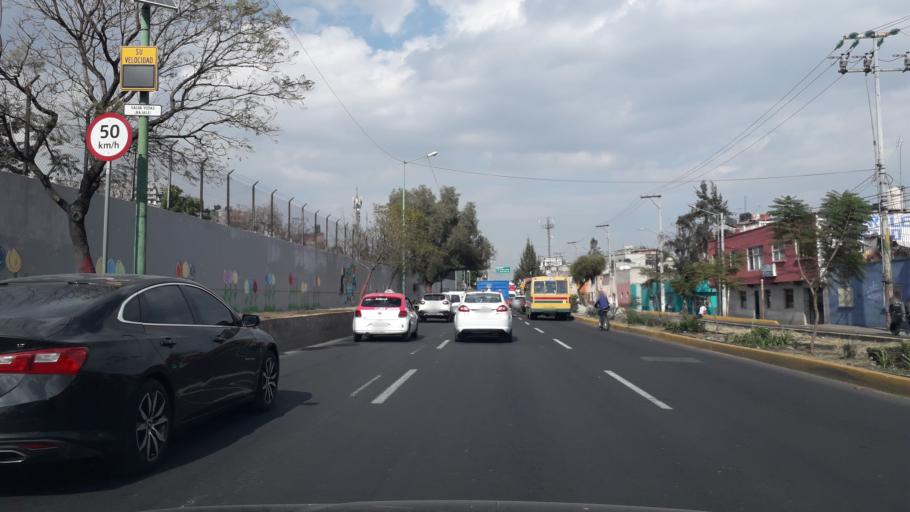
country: MX
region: Mexico City
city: Gustavo A. Madero
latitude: 19.4880
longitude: -99.1019
